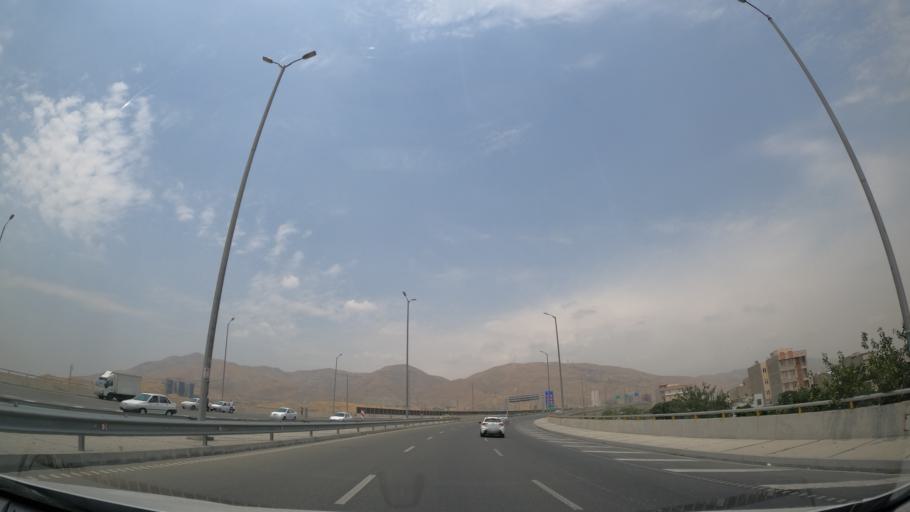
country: IR
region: Tehran
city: Shahr-e Qods
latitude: 35.7375
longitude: 51.1214
